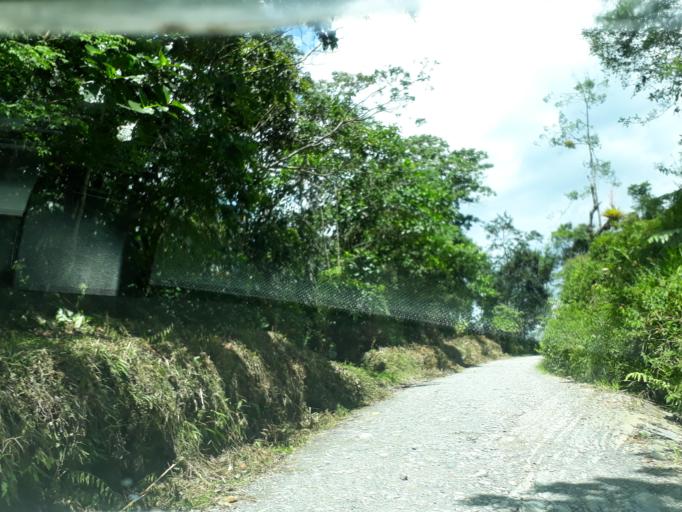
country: CO
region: Cundinamarca
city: Topaipi
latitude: 5.3670
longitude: -74.1967
